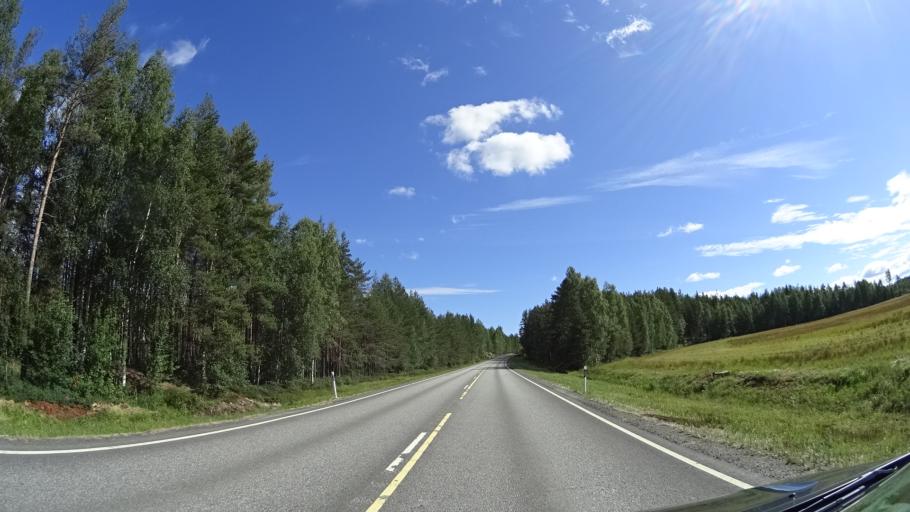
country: FI
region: Pirkanmaa
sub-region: Luoteis-Pirkanmaa
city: Kihnioe
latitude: 62.2163
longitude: 23.2590
